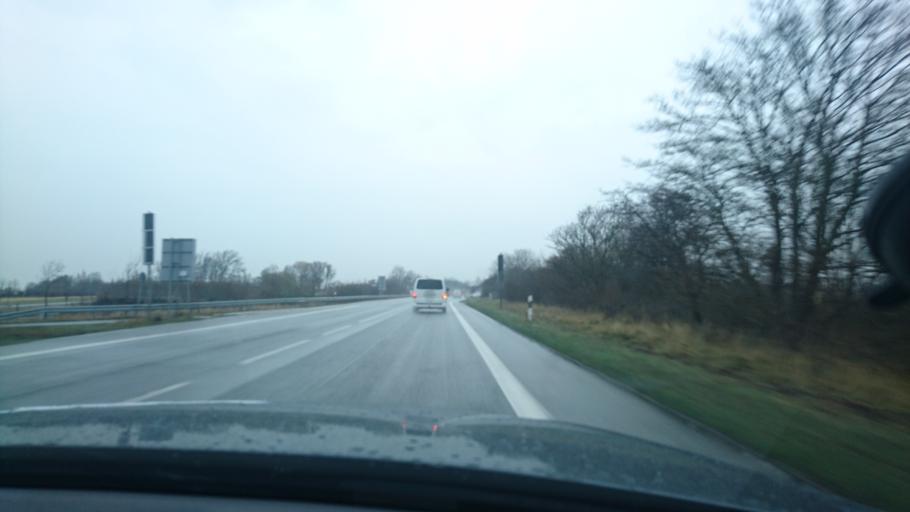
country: DE
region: Schleswig-Holstein
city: Grossenbrode
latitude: 54.4232
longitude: 11.1293
